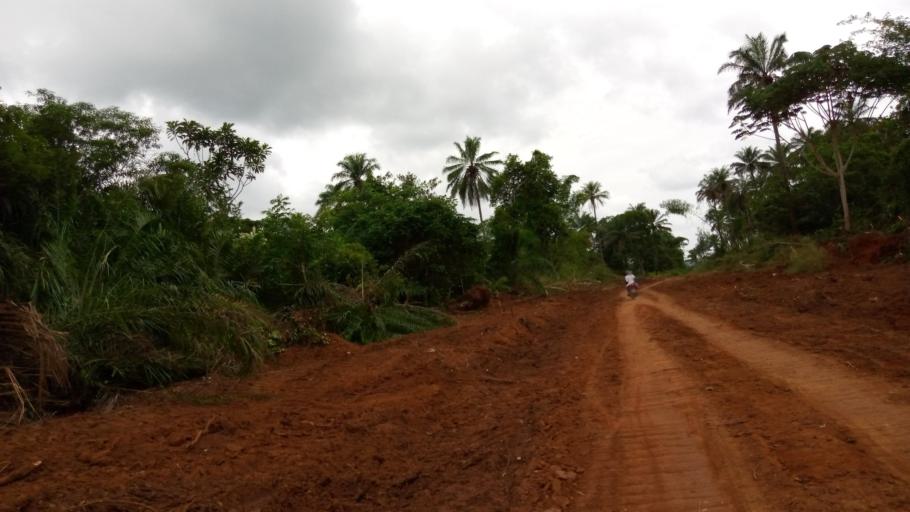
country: SL
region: Southern Province
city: Moyamba
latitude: 8.1951
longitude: -12.5411
